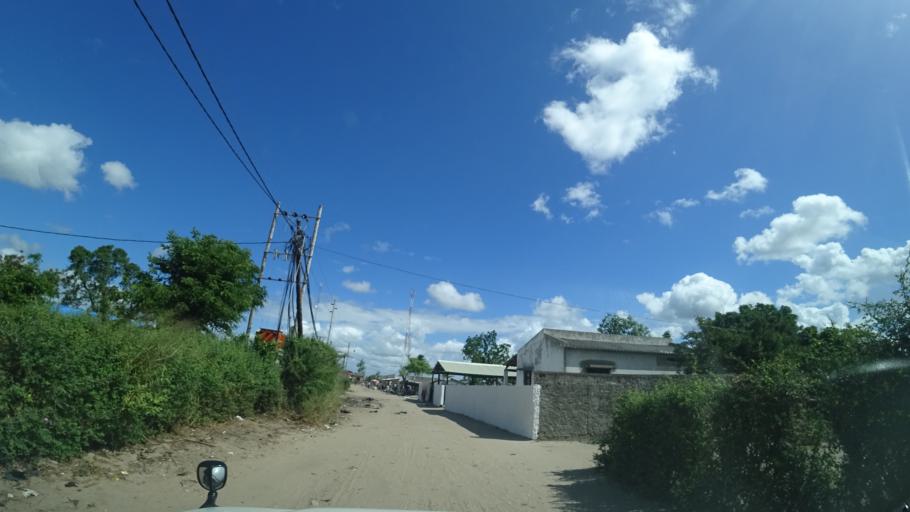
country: MZ
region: Sofala
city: Dondo
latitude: -19.4993
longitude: 34.5974
